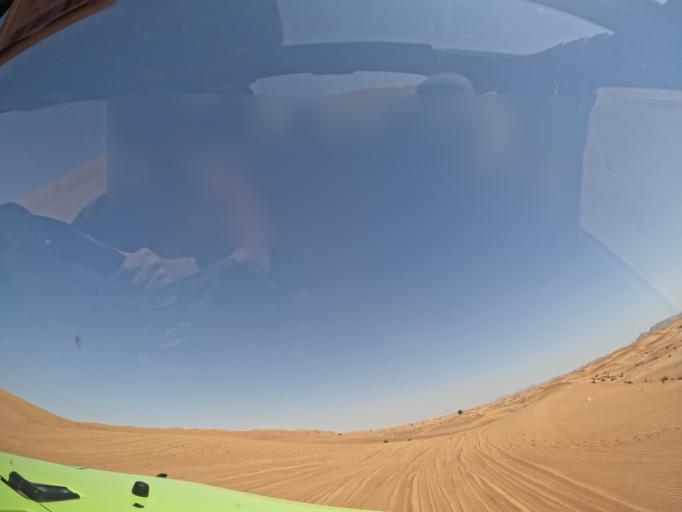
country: AE
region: Ash Shariqah
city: Adh Dhayd
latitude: 24.9919
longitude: 55.7240
